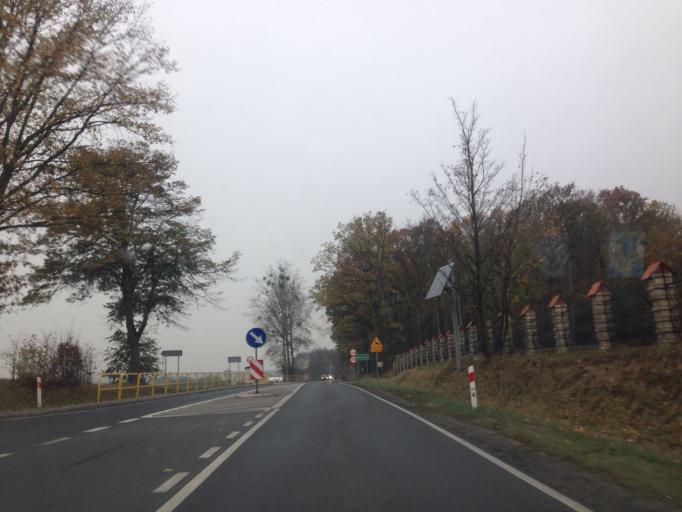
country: PL
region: Kujawsko-Pomorskie
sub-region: Powiat brodnicki
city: Brodnica
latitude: 53.2594
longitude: 19.3584
